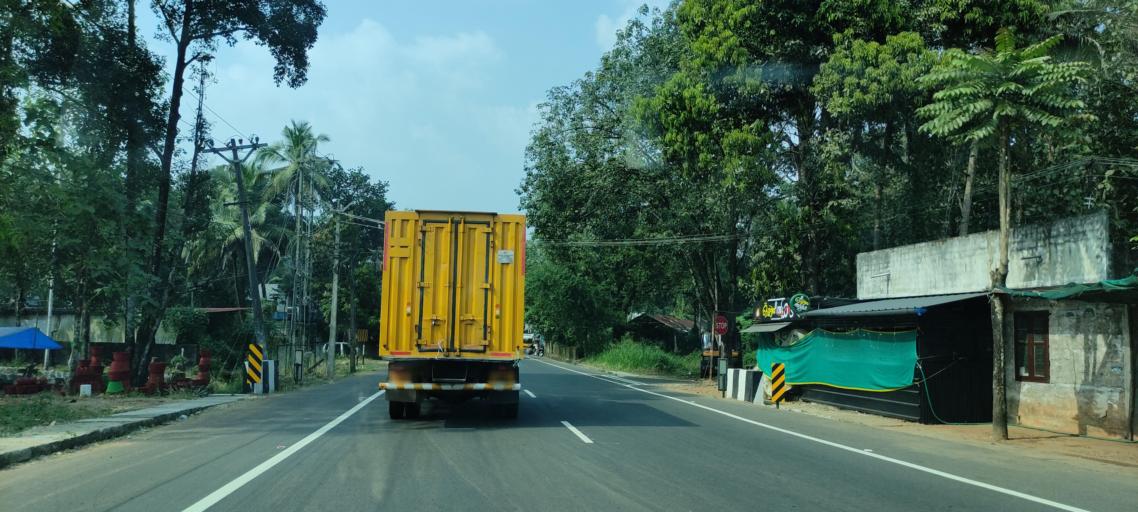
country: IN
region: Kerala
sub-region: Alappuzha
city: Chengannur
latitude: 9.2869
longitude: 76.6519
